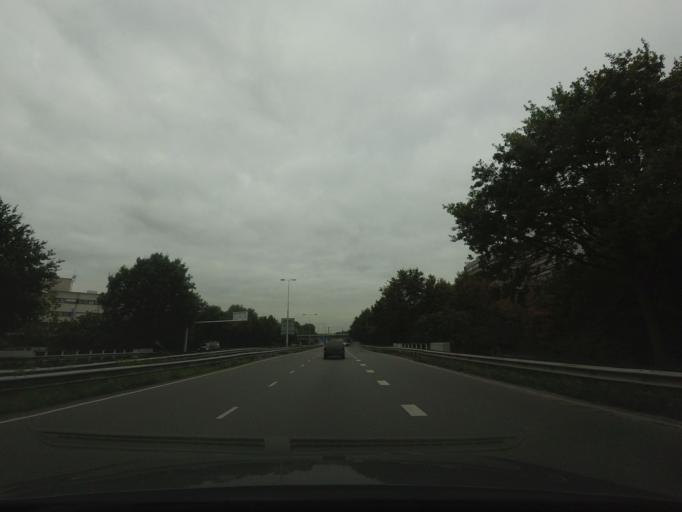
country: NL
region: North Holland
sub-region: Gemeente Ouder-Amstel
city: Duivendrecht
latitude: 52.3272
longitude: 4.9542
